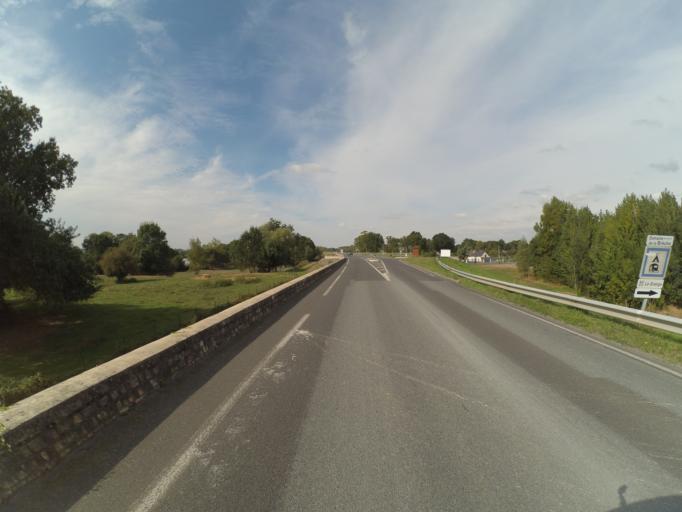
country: FR
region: Pays de la Loire
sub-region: Departement de Maine-et-Loire
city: Villebernier
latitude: 47.2447
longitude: 0.0029
